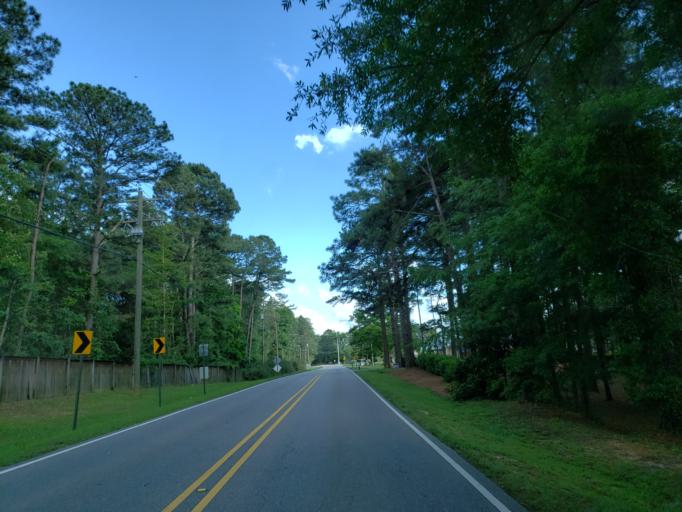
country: US
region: Mississippi
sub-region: Lamar County
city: West Hattiesburg
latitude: 31.2839
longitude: -89.4369
